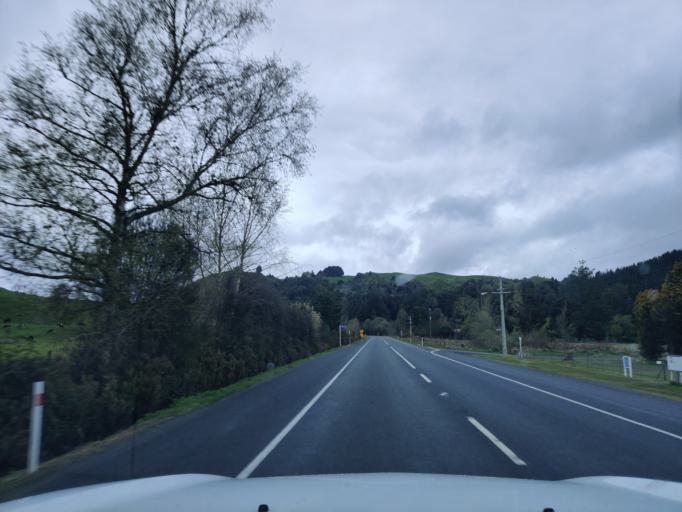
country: NZ
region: Waikato
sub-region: Otorohanga District
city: Otorohanga
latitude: -38.5760
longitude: 175.2139
